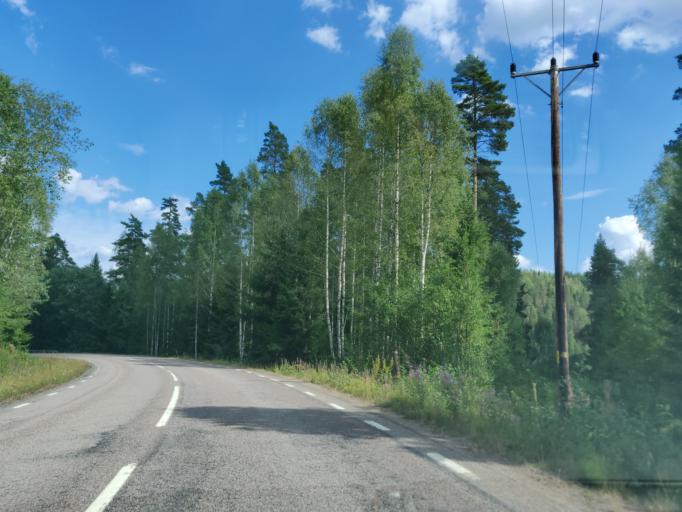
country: SE
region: Vaermland
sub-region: Munkfors Kommun
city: Munkfors
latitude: 59.8548
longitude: 13.6478
